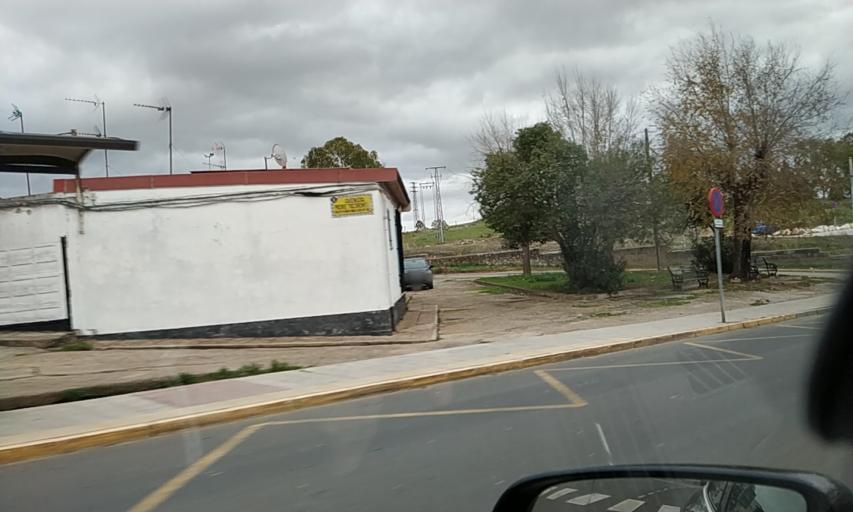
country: ES
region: Extremadura
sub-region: Provincia de Badajoz
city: Badajoz
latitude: 38.8899
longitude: -6.9762
